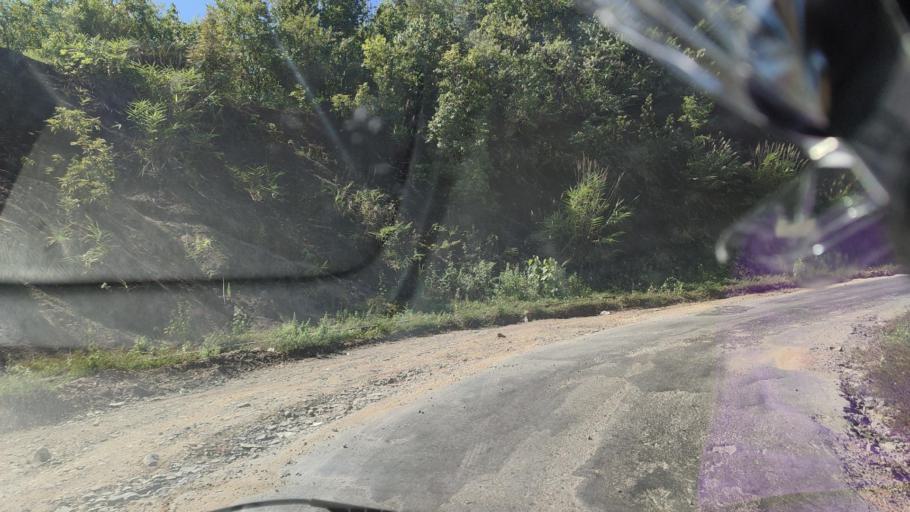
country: MM
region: Rakhine
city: Sittwe
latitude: 19.9821
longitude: 93.6347
